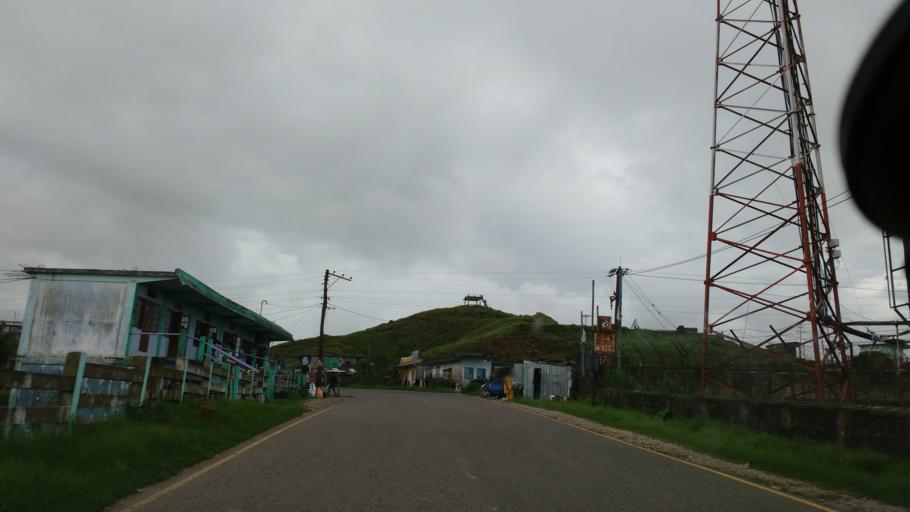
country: IN
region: Meghalaya
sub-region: East Khasi Hills
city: Cherrapunji
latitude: 25.2724
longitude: 91.7327
